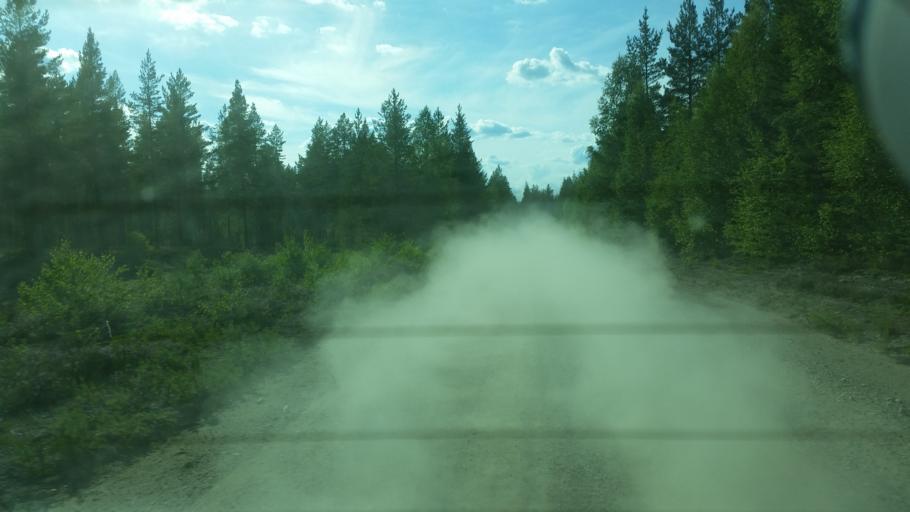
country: SE
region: Vaesternorrland
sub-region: Ange Kommun
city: Ange
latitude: 62.2003
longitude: 15.5672
